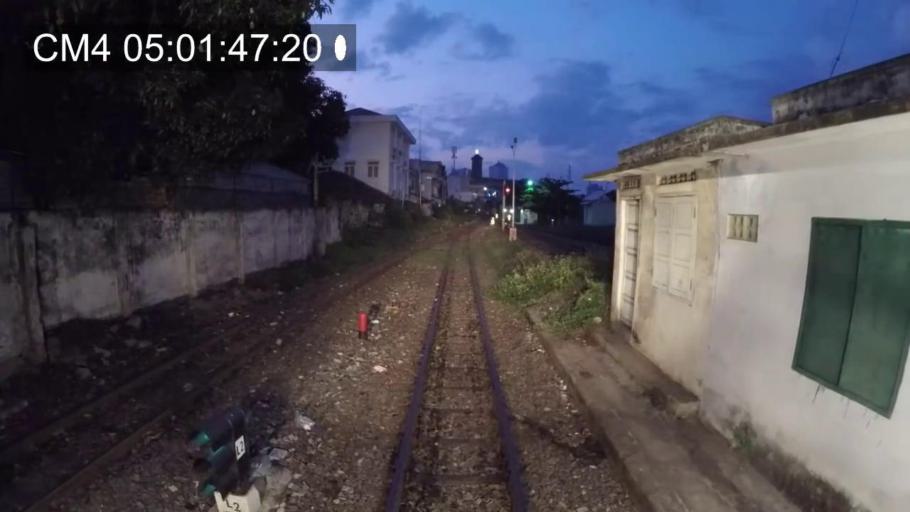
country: VN
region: Khanh Hoa
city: Nha Trang
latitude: 12.2493
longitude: 109.1812
